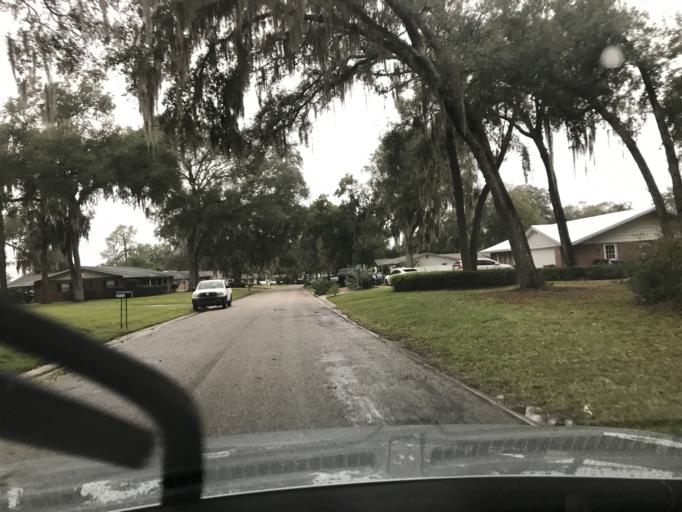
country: US
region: Florida
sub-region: Hillsborough County
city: Plant City
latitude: 28.0380
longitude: -82.0978
